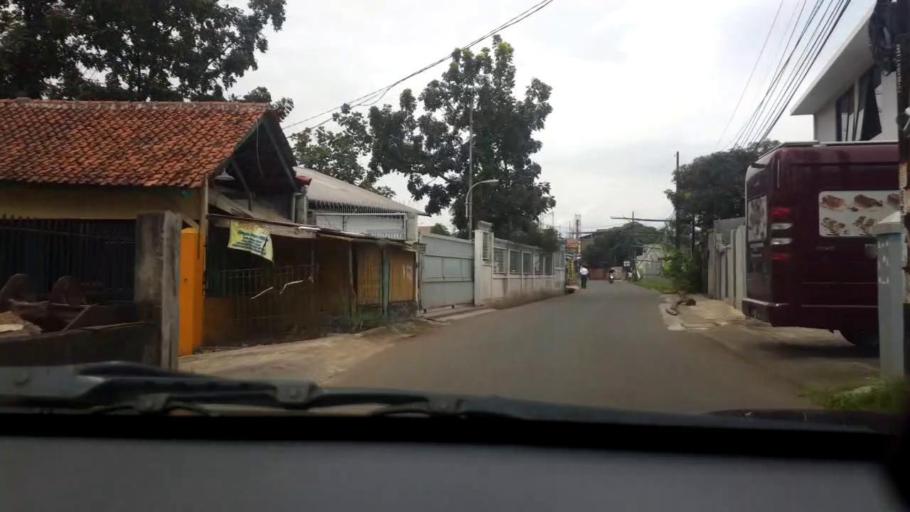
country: ID
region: West Java
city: Cileunyi
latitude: -6.9357
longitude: 107.7268
